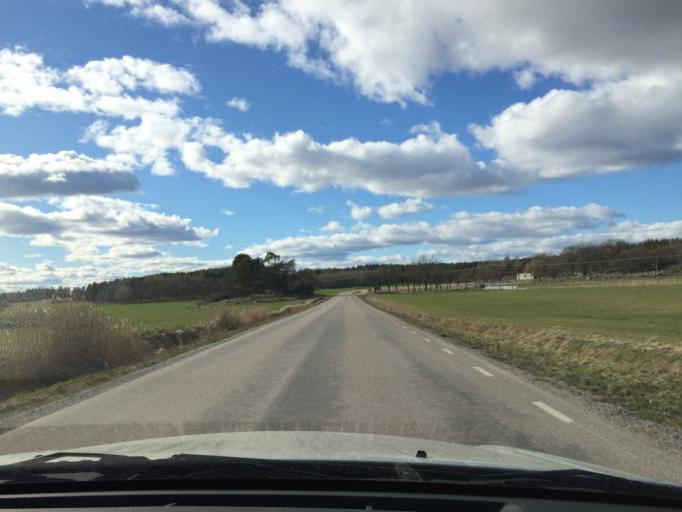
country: SE
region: Soedermanland
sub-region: Eskilstuna Kommun
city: Torshalla
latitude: 59.4153
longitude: 16.4433
